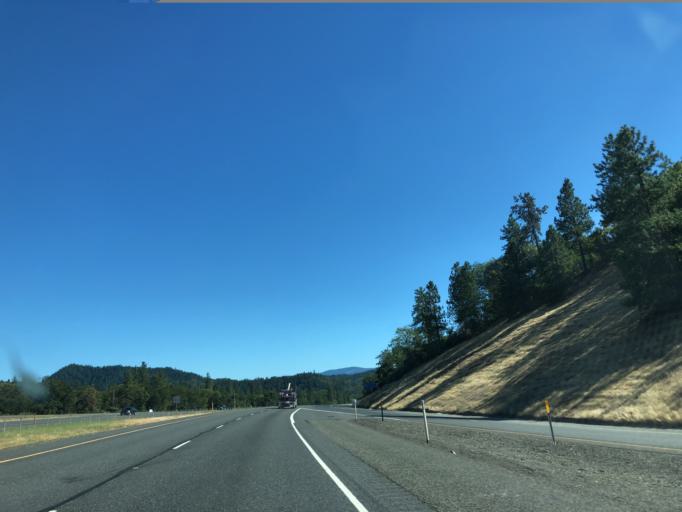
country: US
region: Oregon
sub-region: Josephine County
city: Merlin
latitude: 42.5151
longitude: -123.3639
